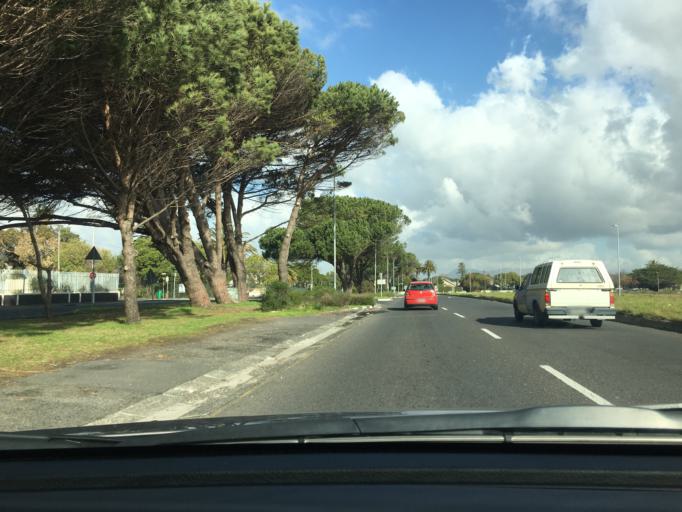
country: ZA
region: Western Cape
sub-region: City of Cape Town
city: Rondebosch
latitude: -33.9571
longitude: 18.4857
